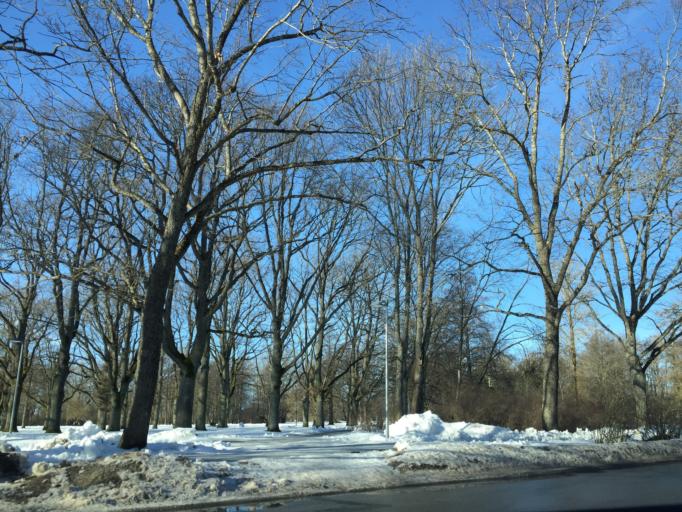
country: EE
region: Paernumaa
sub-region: Paernu linn
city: Parnu
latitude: 58.3784
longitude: 24.4927
